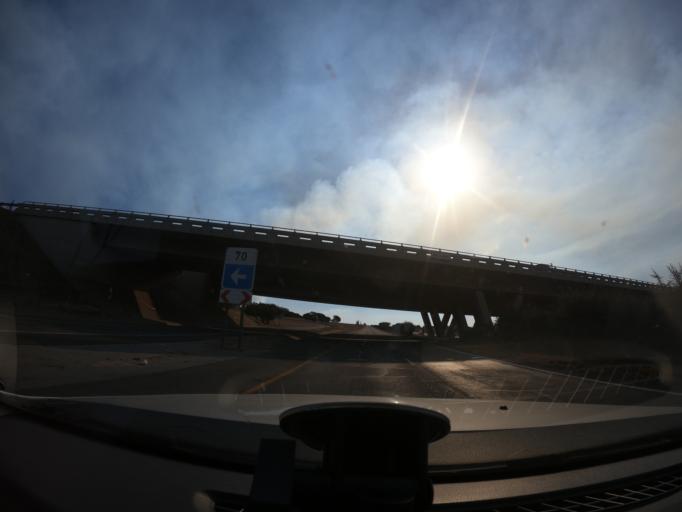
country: ZA
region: Gauteng
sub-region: Sedibeng District Municipality
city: Heidelberg
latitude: -26.4687
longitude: 28.3419
